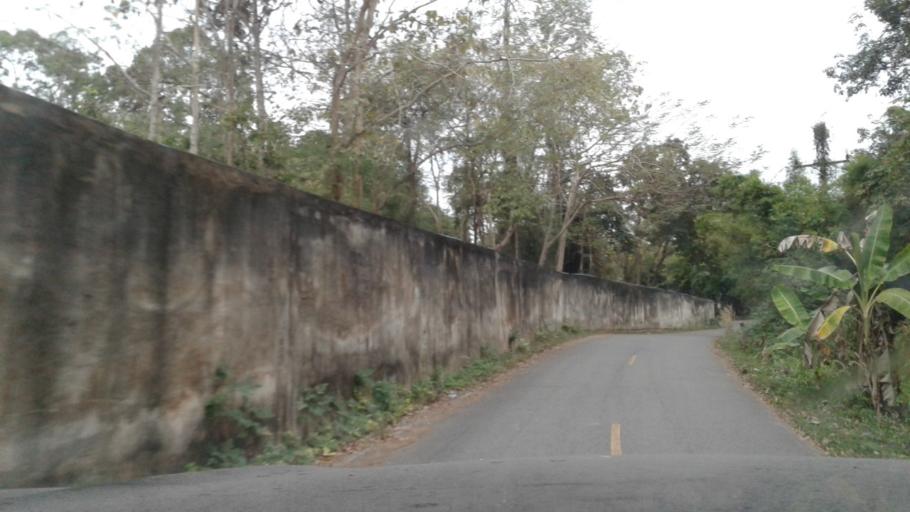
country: TH
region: Changwat Udon Thani
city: Nong Wua So
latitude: 17.2285
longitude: 102.5344
